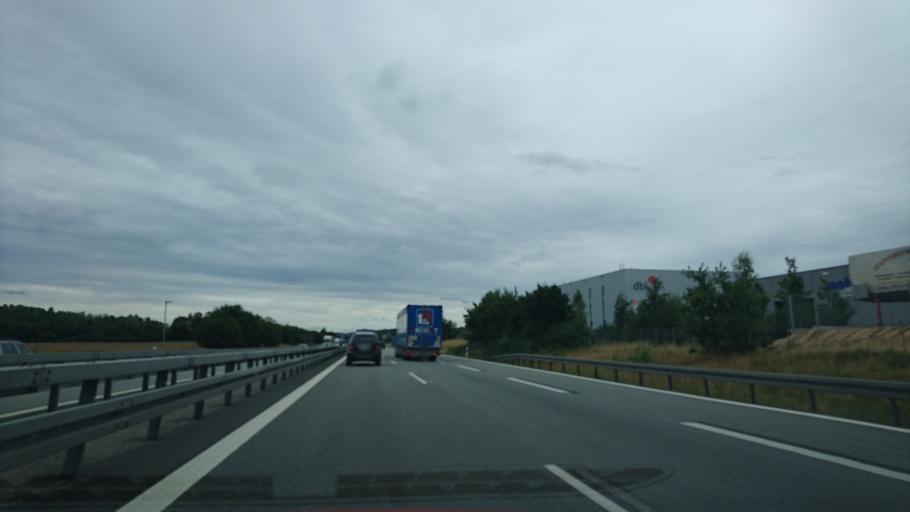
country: DE
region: Bavaria
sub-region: Upper Palatinate
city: Pfreimd
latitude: 49.4779
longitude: 12.1911
